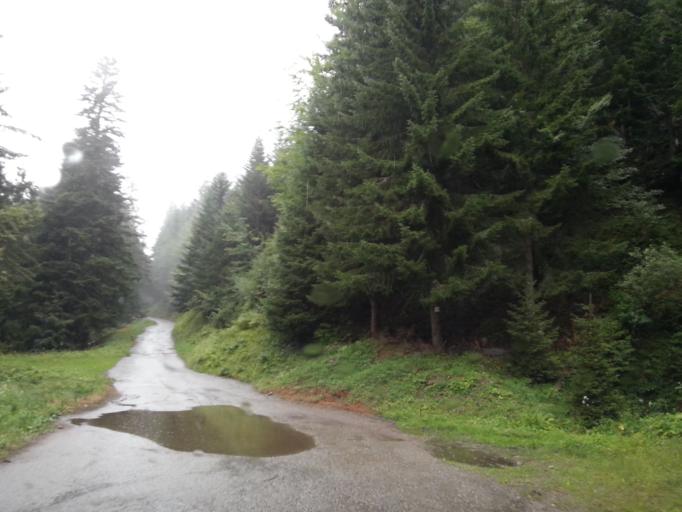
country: FR
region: Rhone-Alpes
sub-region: Departement de la Savoie
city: Marthod
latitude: 45.6976
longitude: 6.4484
